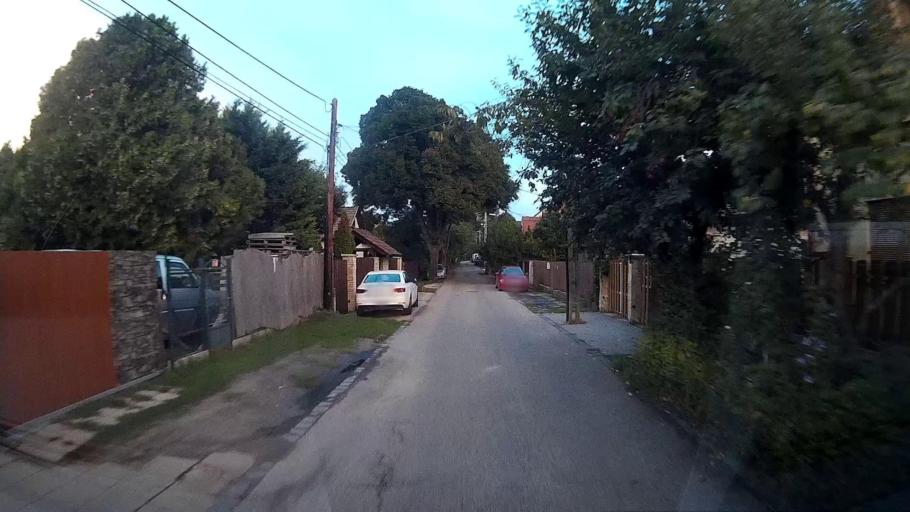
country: HU
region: Pest
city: Budakalasz
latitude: 47.5898
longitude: 19.0523
